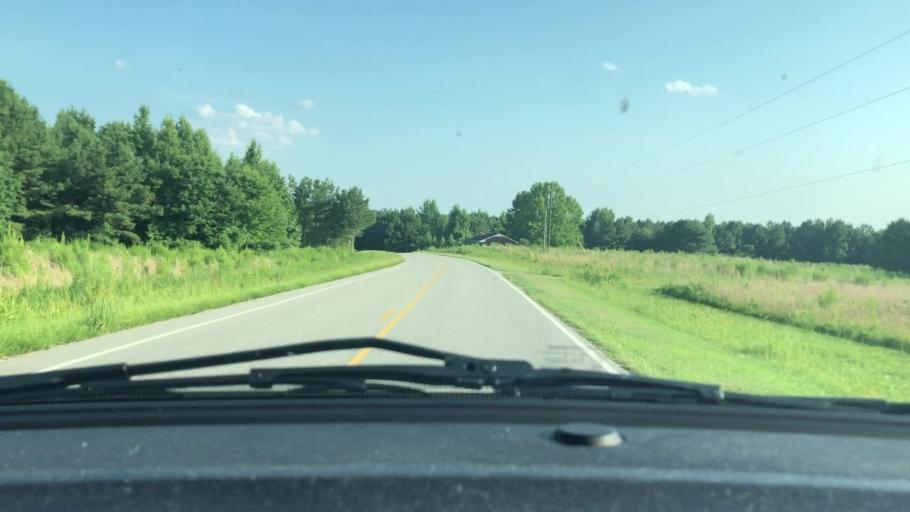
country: US
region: North Carolina
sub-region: Lee County
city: Broadway
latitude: 35.3378
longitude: -79.0731
